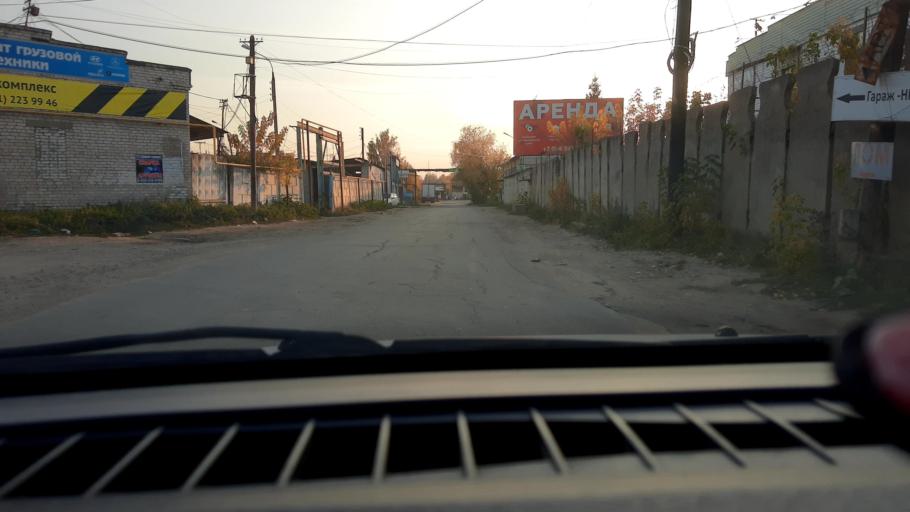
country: RU
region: Nizjnij Novgorod
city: Gorbatovka
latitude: 56.3092
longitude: 43.8257
